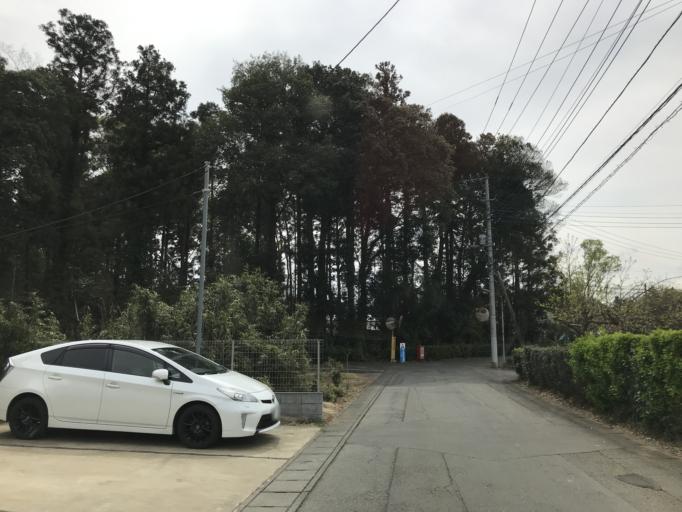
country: JP
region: Ibaraki
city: Moriya
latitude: 35.9525
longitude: 140.0139
